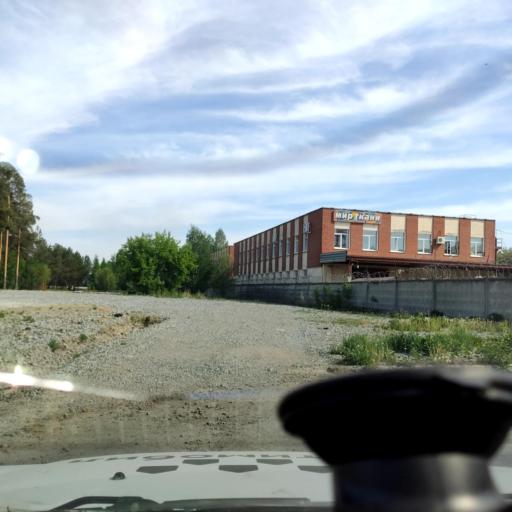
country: RU
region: Sverdlovsk
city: Sovkhoznyy
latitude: 56.7710
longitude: 60.5593
